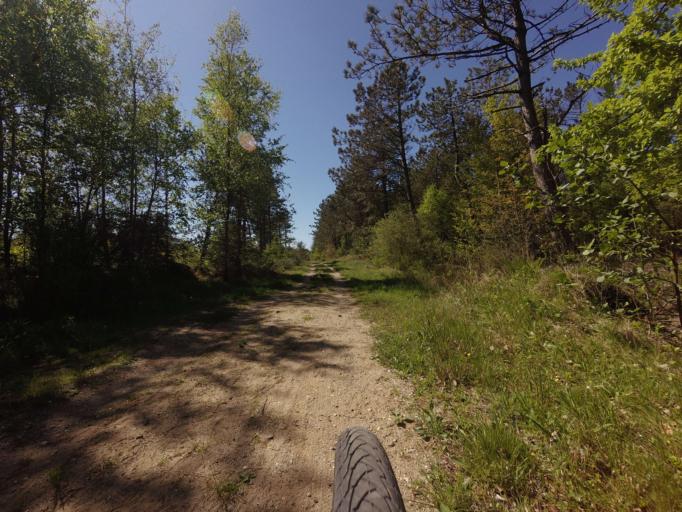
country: DK
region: North Denmark
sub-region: Jammerbugt Kommune
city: Pandrup
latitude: 57.2777
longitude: 9.6330
